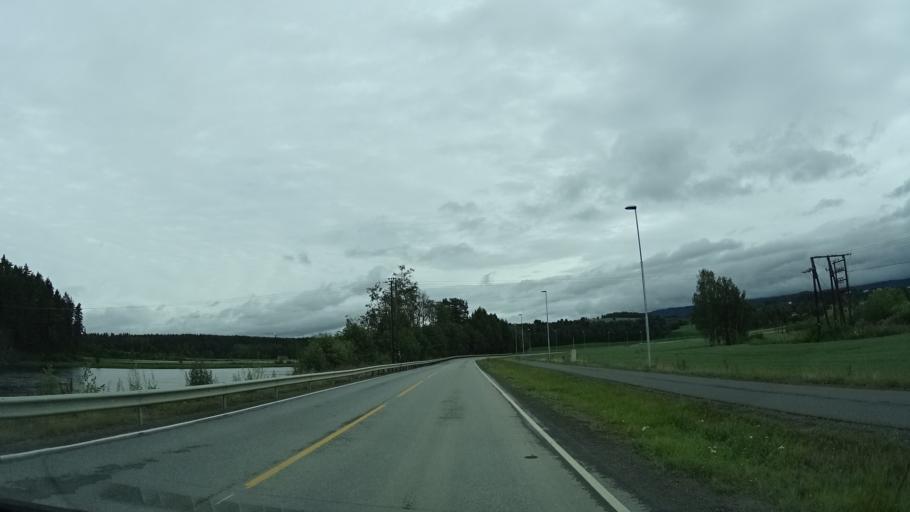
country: NO
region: Buskerud
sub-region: Ringerike
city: Honefoss
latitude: 60.1267
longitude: 10.2474
